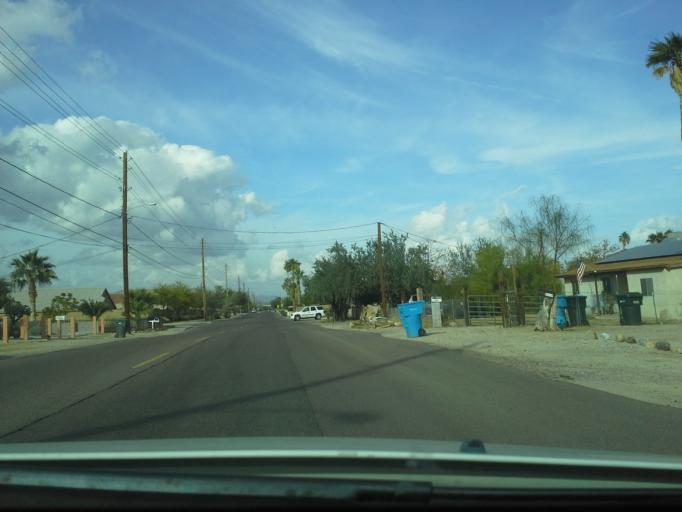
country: US
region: Arizona
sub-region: Maricopa County
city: Phoenix
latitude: 33.3659
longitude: -112.0833
